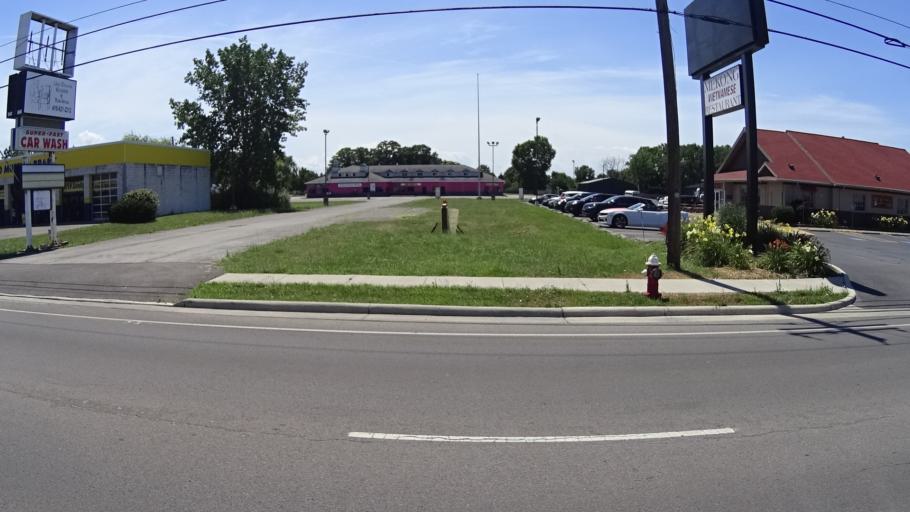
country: US
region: Ohio
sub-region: Erie County
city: Sandusky
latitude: 41.4259
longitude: -82.6818
